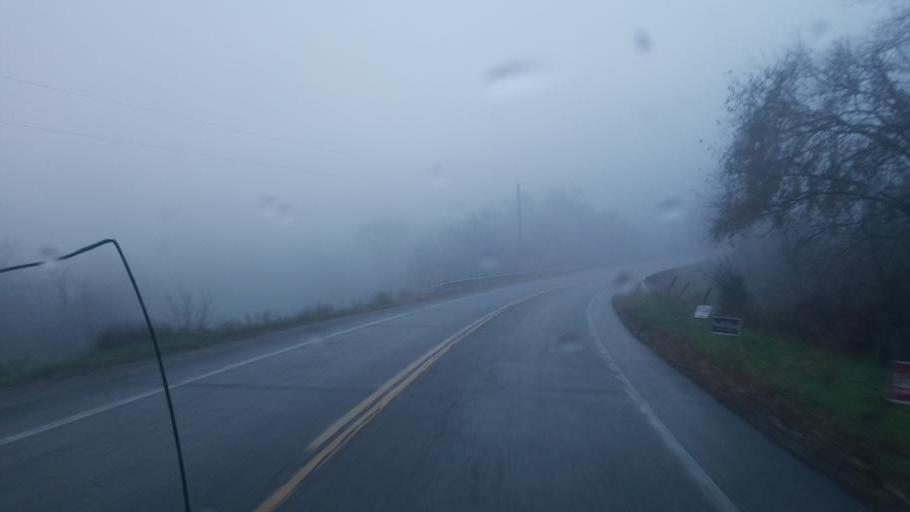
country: US
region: Ohio
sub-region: Morgan County
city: McConnelsville
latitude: 39.5026
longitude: -81.8558
